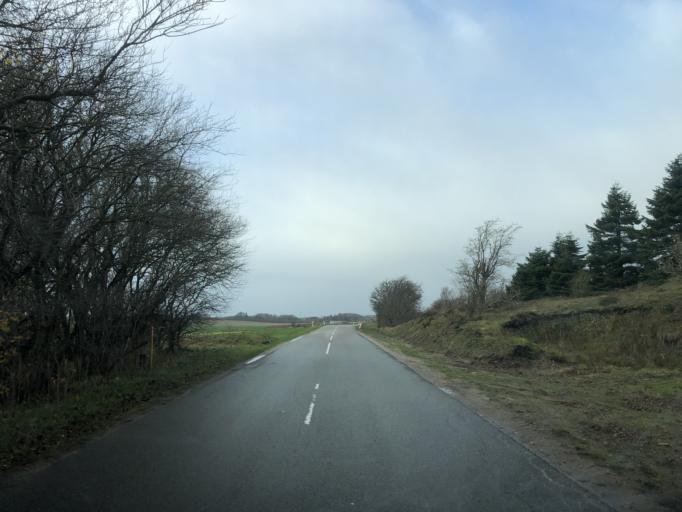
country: DK
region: North Denmark
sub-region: Rebild Kommune
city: Stovring
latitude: 56.9138
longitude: 9.7985
